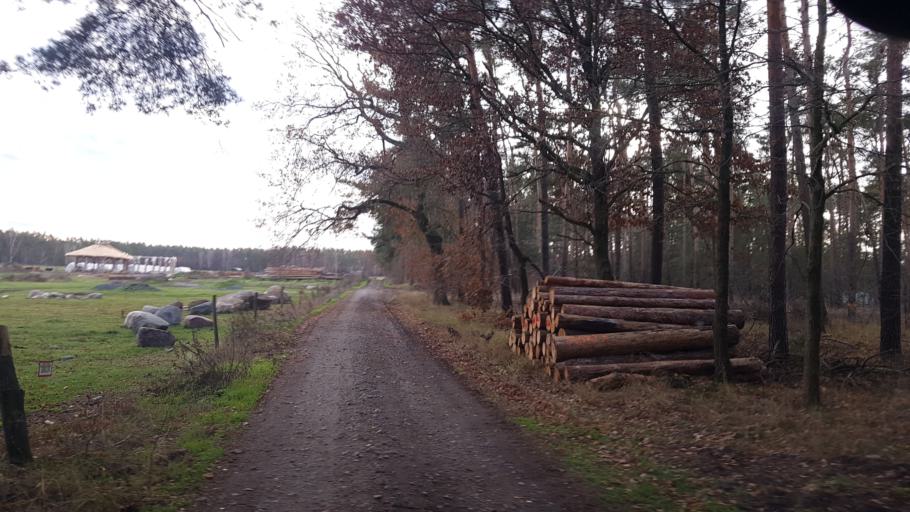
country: DE
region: Brandenburg
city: Falkenberg
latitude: 51.5731
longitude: 13.2778
